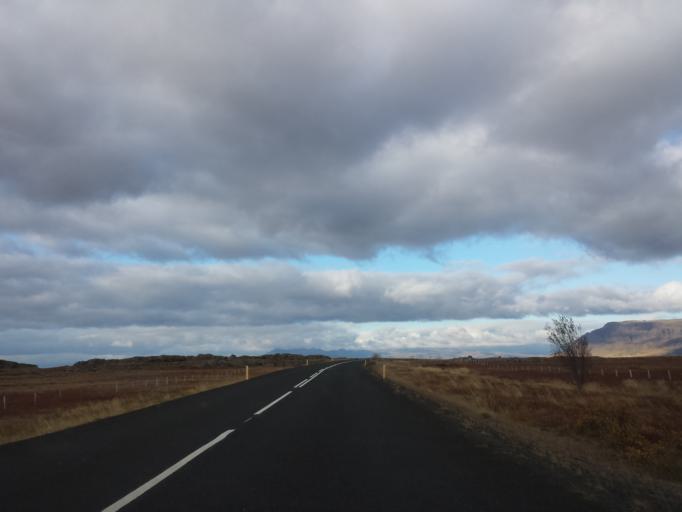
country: IS
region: West
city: Borgarnes
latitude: 64.6864
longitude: -22.0922
